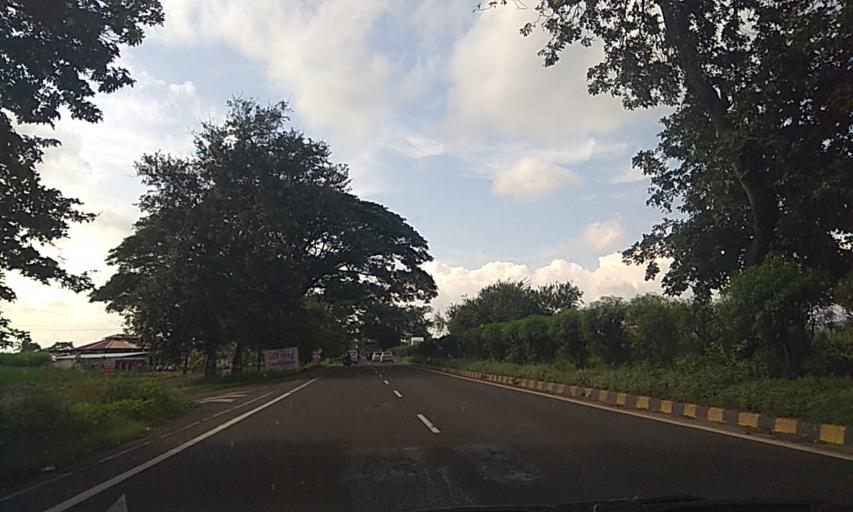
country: IN
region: Maharashtra
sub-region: Kolhapur
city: Kodoli
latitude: 16.9291
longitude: 74.2870
